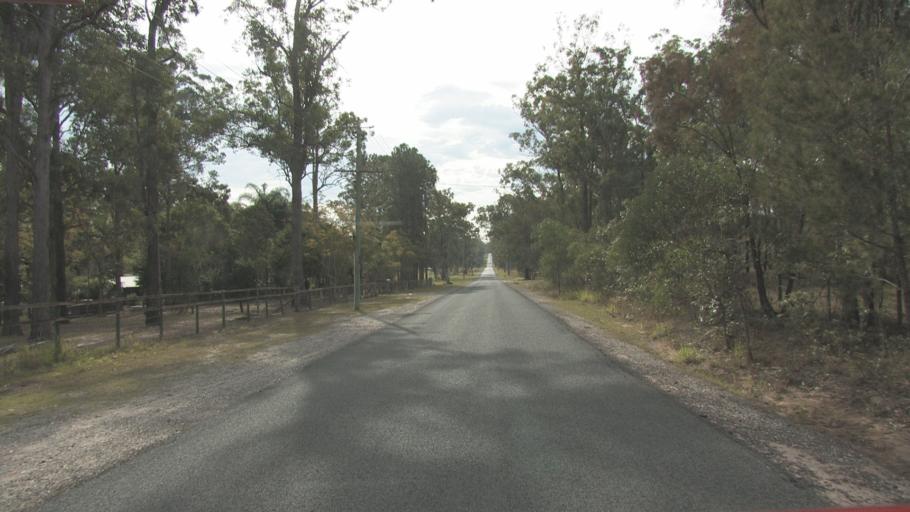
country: AU
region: Queensland
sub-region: Logan
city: Chambers Flat
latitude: -27.7925
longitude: 153.1212
